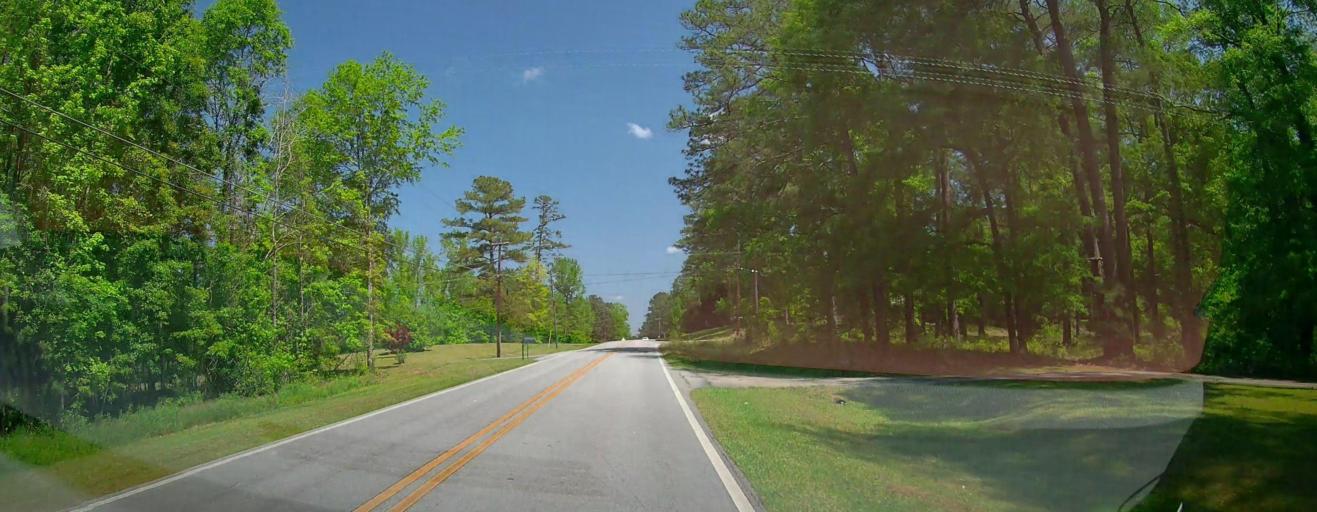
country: US
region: Georgia
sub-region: Bibb County
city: Macon
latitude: 32.8915
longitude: -83.6094
